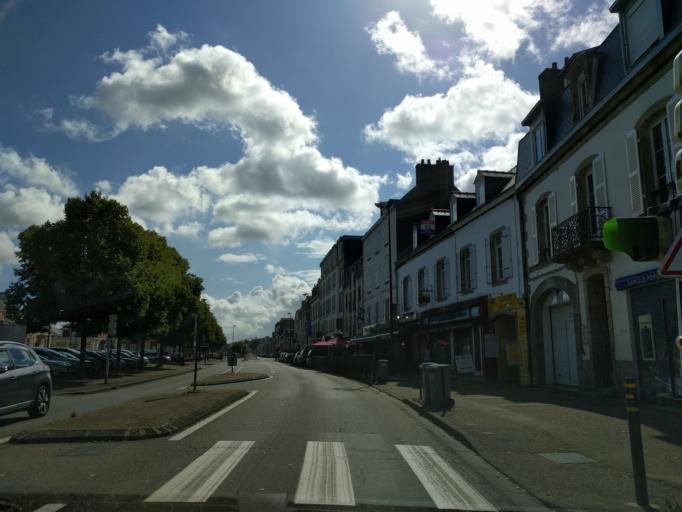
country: FR
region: Brittany
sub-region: Departement du Finistere
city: Quimper
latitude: 47.9943
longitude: -4.0938
